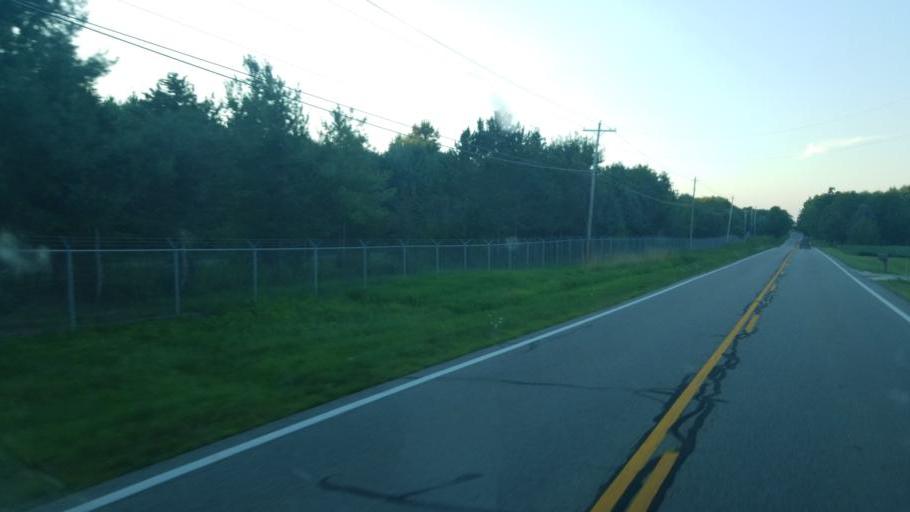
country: US
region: Ohio
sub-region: Trumbull County
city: Newton Falls
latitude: 41.2154
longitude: -80.9798
